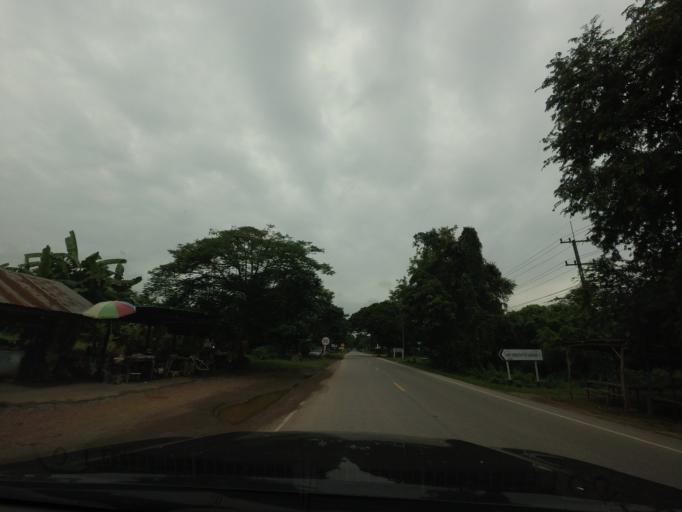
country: TH
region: Nong Khai
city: Si Chiang Mai
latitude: 17.9611
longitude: 102.5205
